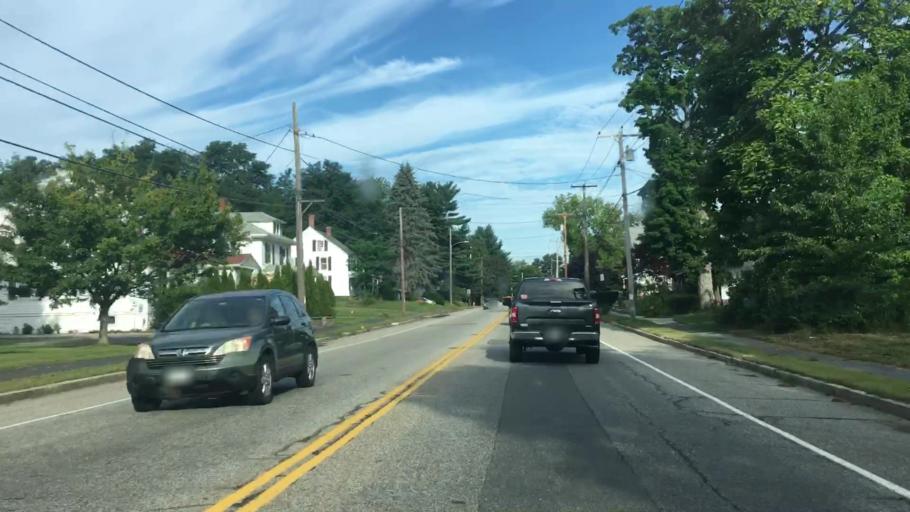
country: US
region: Maine
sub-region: Cumberland County
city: Portland
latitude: 43.6914
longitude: -70.2792
